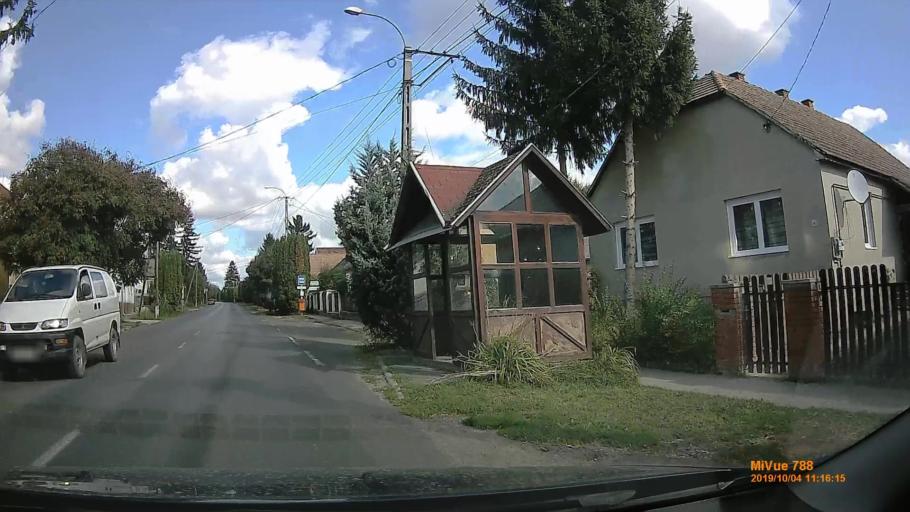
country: HU
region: Somogy
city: Kaposvar
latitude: 46.4541
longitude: 17.8053
